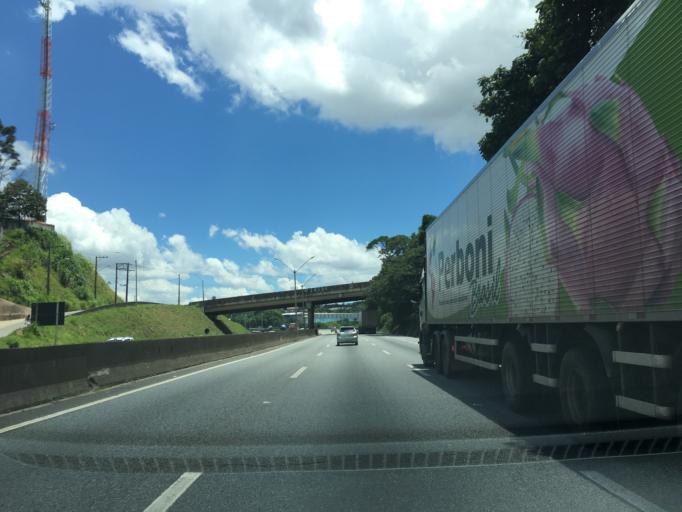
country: BR
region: Sao Paulo
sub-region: Guarulhos
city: Guarulhos
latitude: -23.4090
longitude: -46.5810
